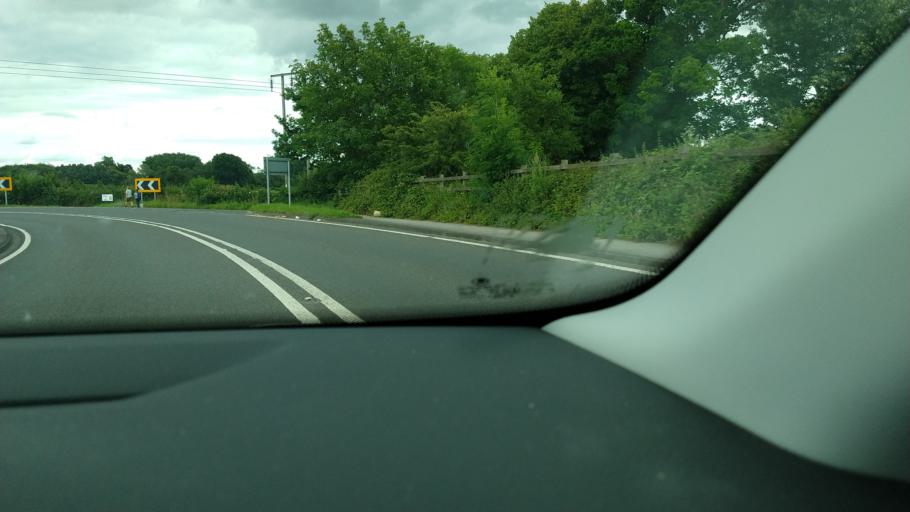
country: GB
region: England
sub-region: East Riding of Yorkshire
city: Snaith
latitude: 53.6993
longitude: -1.0239
